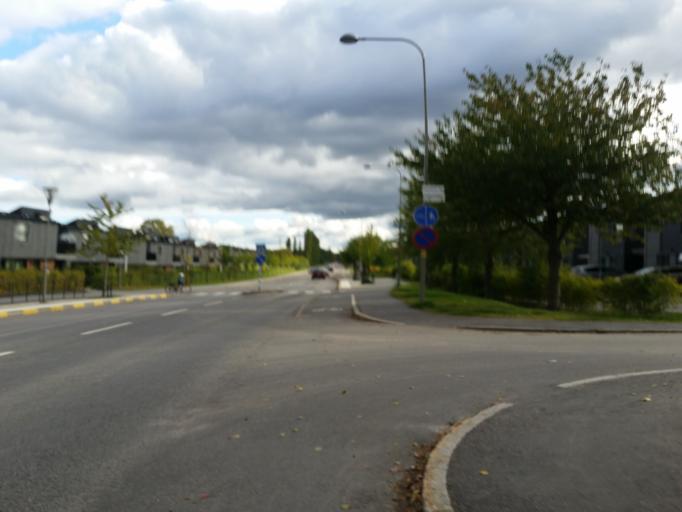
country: SE
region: Stockholm
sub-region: Nacka Kommun
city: Nacka
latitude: 59.2713
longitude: 18.1113
